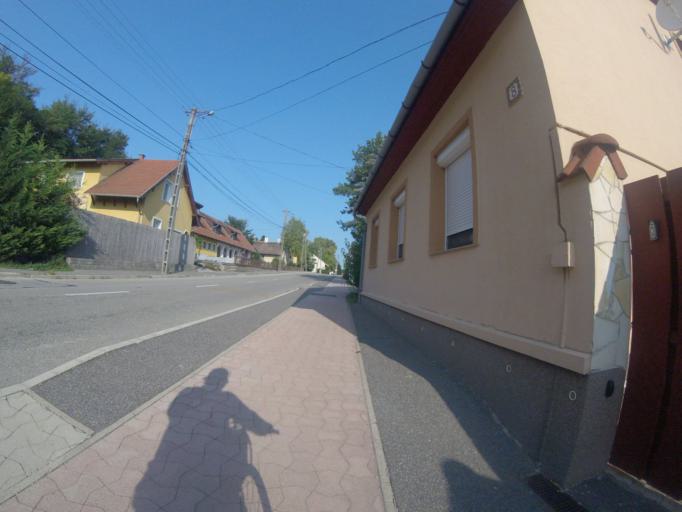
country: HU
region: Gyor-Moson-Sopron
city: Nagycenk
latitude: 47.6261
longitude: 16.7428
